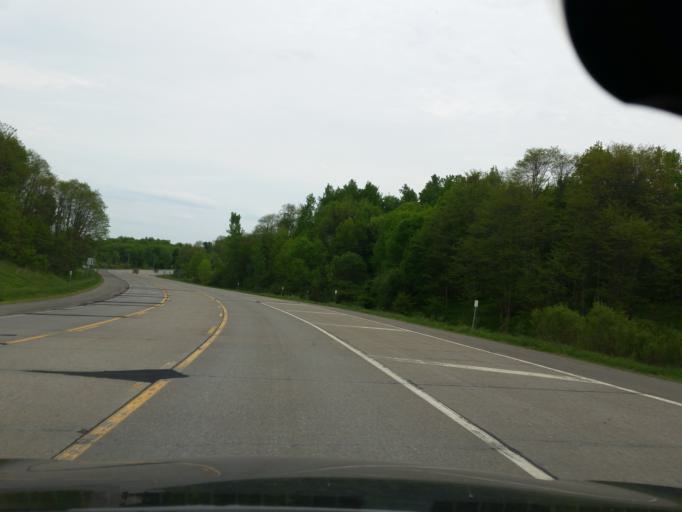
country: US
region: New York
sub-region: Chautauqua County
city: Lakewood
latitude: 42.1489
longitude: -79.4064
